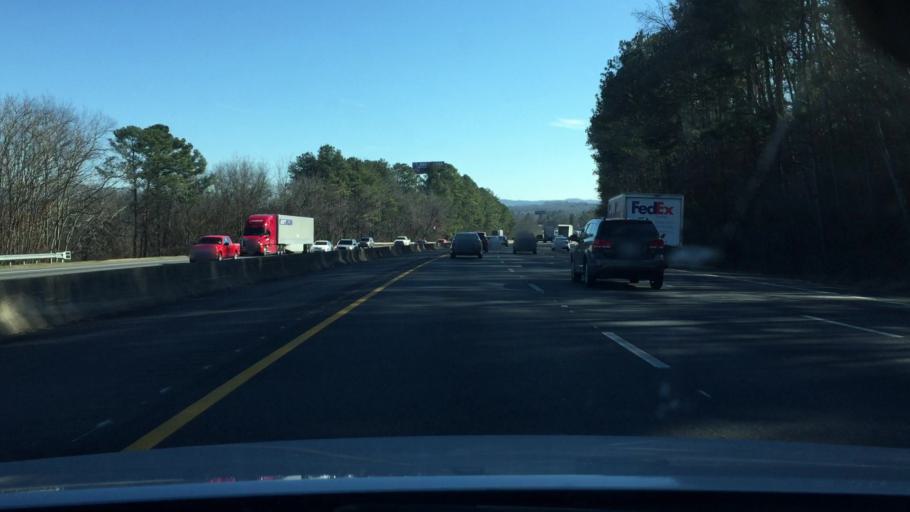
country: US
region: Georgia
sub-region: Catoosa County
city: Ringgold
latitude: 34.9019
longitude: -85.0874
